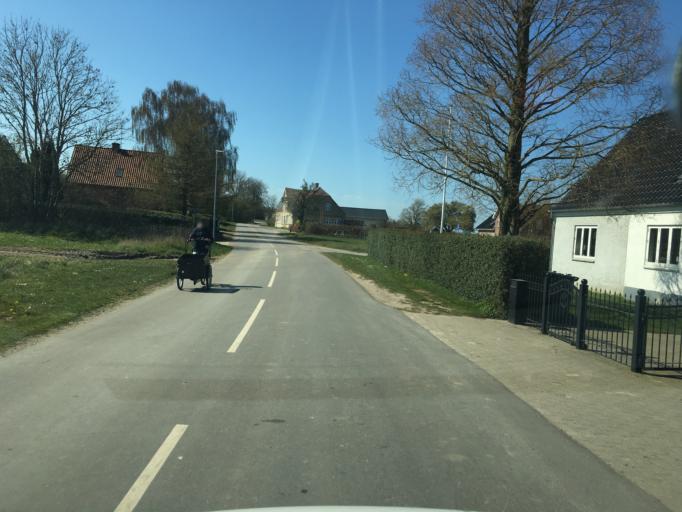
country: DK
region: South Denmark
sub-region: Sonderborg Kommune
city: Dybbol
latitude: 54.9520
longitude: 9.7187
